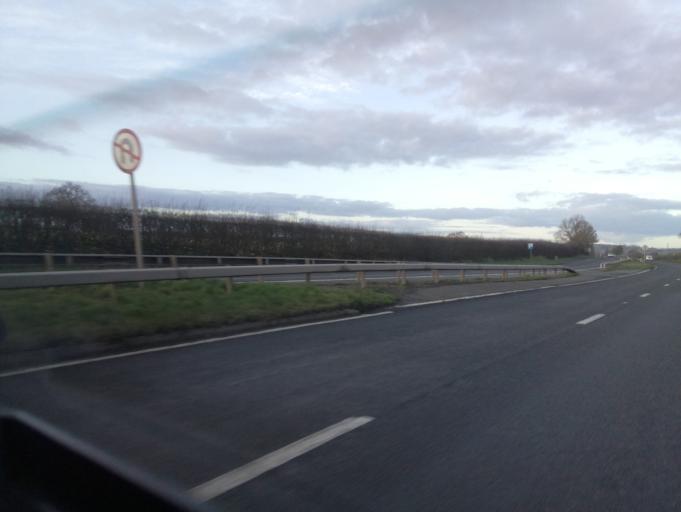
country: GB
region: England
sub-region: Staffordshire
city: Stone
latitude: 52.8685
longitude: -2.1304
